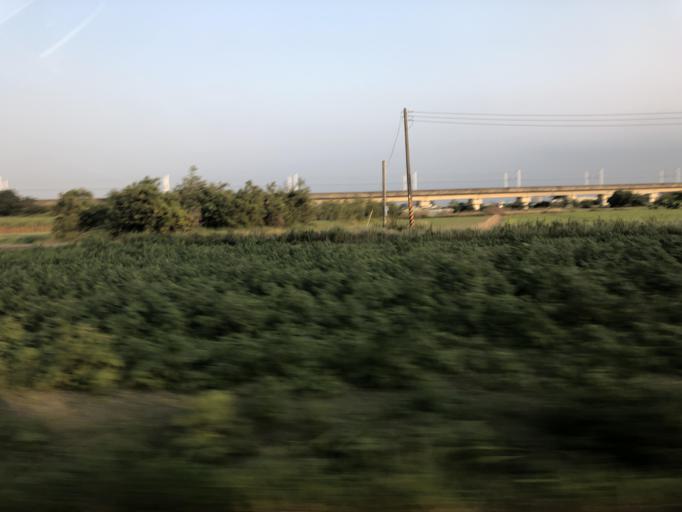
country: TW
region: Taiwan
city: Xinying
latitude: 23.1519
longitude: 120.2750
